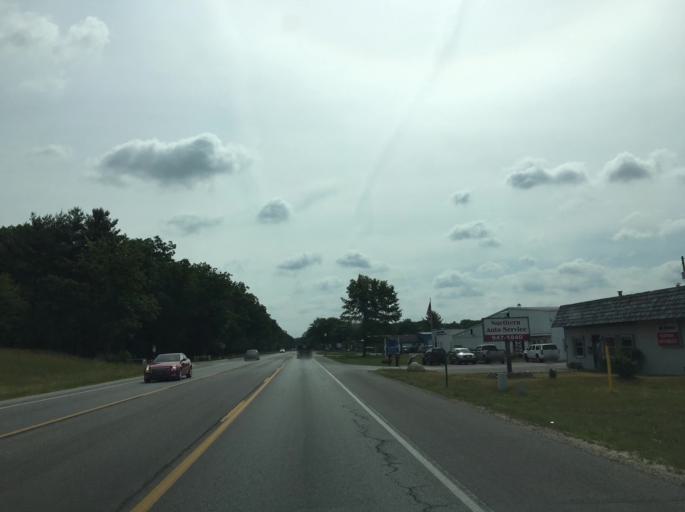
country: US
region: Michigan
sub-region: Grand Traverse County
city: Traverse City
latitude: 44.7333
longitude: -85.5860
